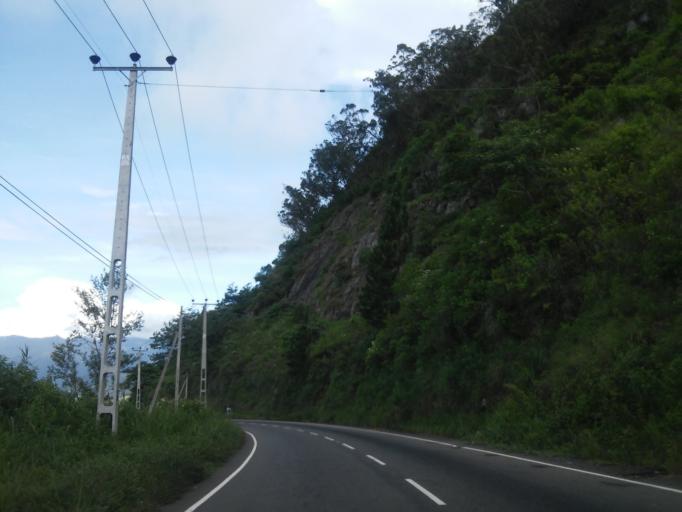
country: LK
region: Uva
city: Haputale
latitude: 6.7607
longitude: 80.9364
